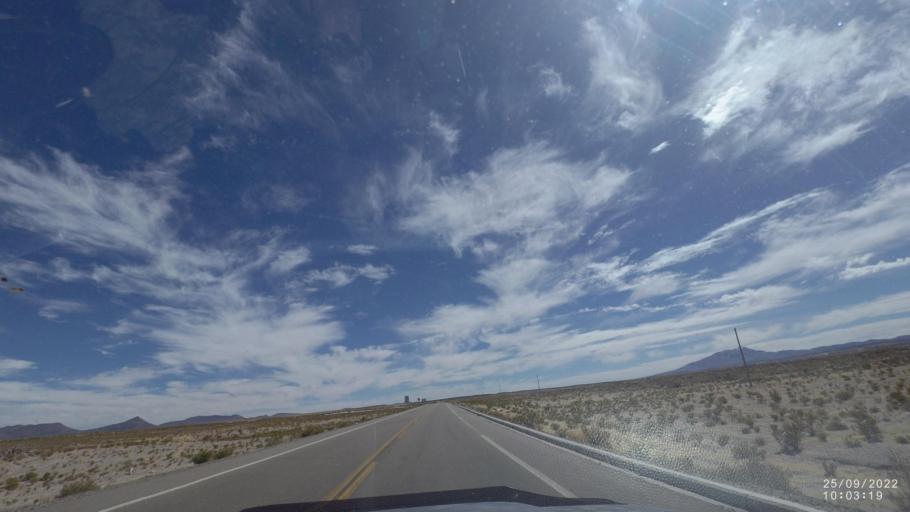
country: BO
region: Potosi
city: Colchani
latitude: -20.2198
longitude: -66.9564
